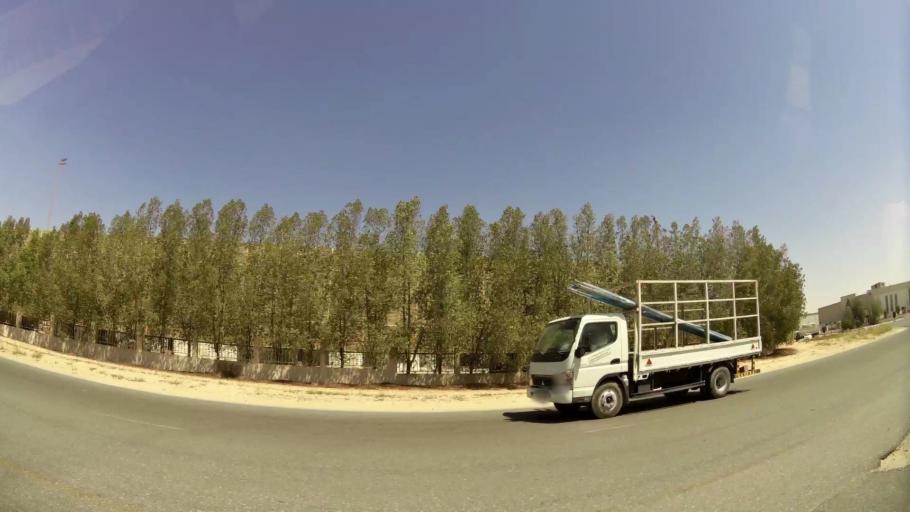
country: AE
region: Dubai
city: Dubai
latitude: 24.9792
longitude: 55.2083
